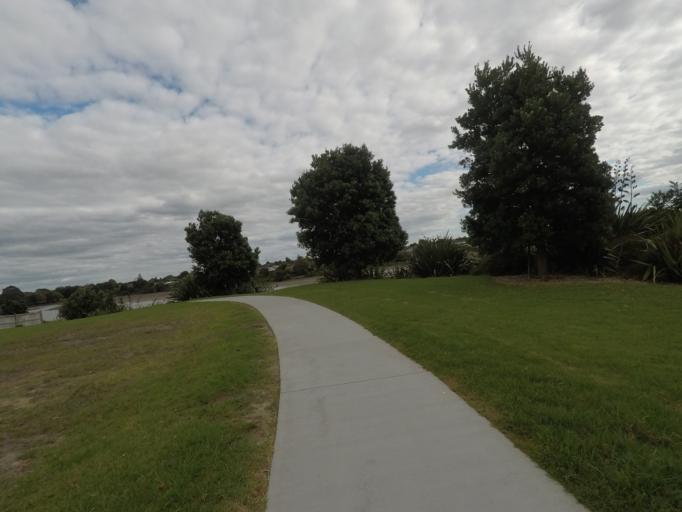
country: NZ
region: Auckland
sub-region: Auckland
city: Papakura
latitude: -37.0599
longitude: 174.9308
